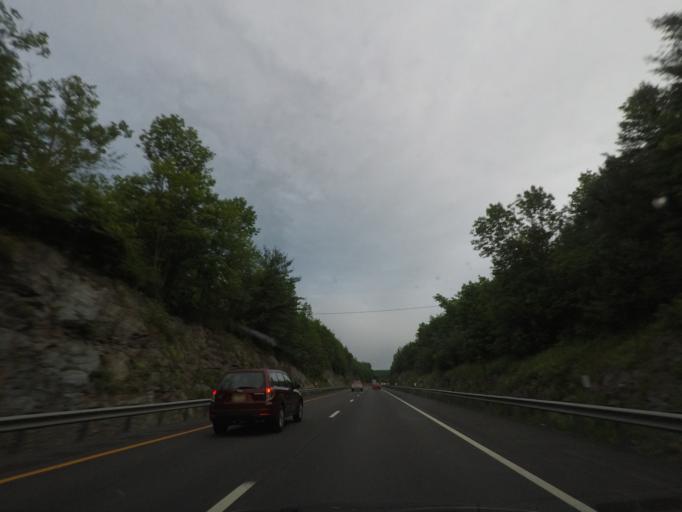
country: US
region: New York
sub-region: Columbia County
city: Chatham
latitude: 42.4296
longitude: -73.5525
